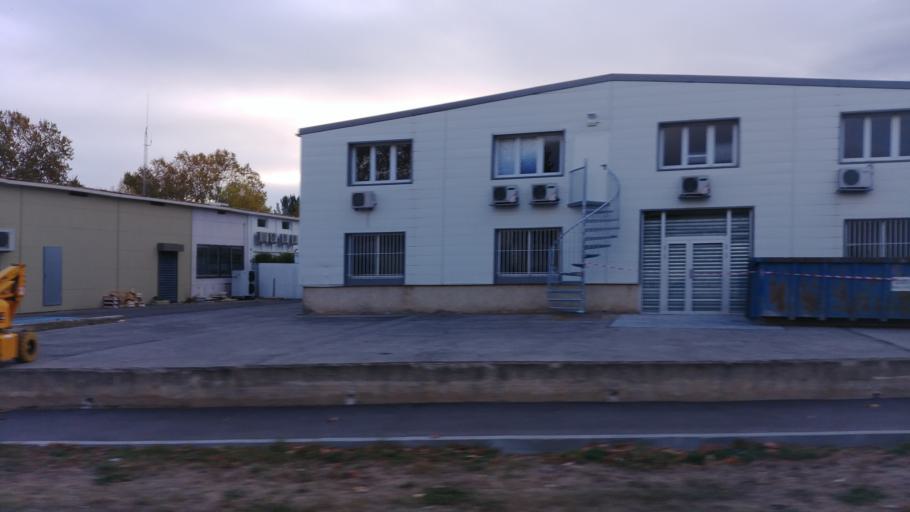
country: FR
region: Provence-Alpes-Cote d'Azur
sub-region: Departement des Bouches-du-Rhone
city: Venelles
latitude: 43.5853
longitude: 5.4745
